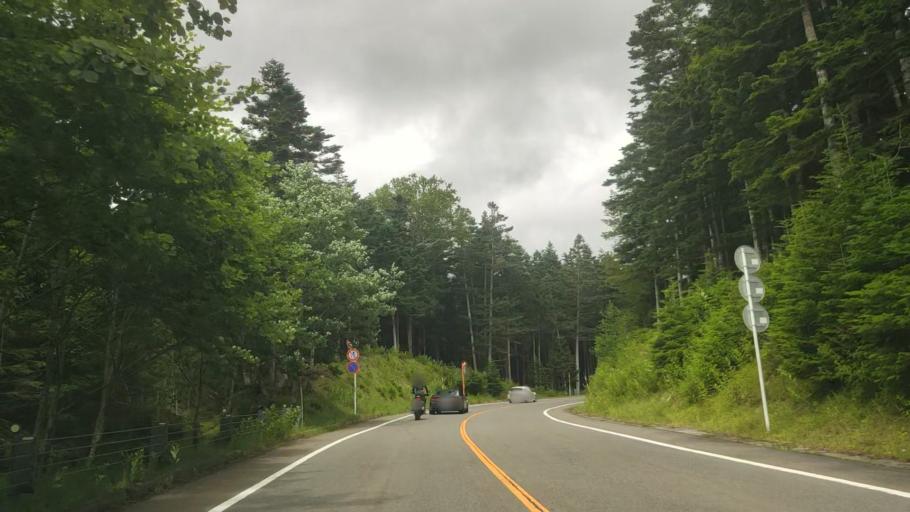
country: JP
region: Tochigi
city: Nikko
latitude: 36.8145
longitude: 139.3509
